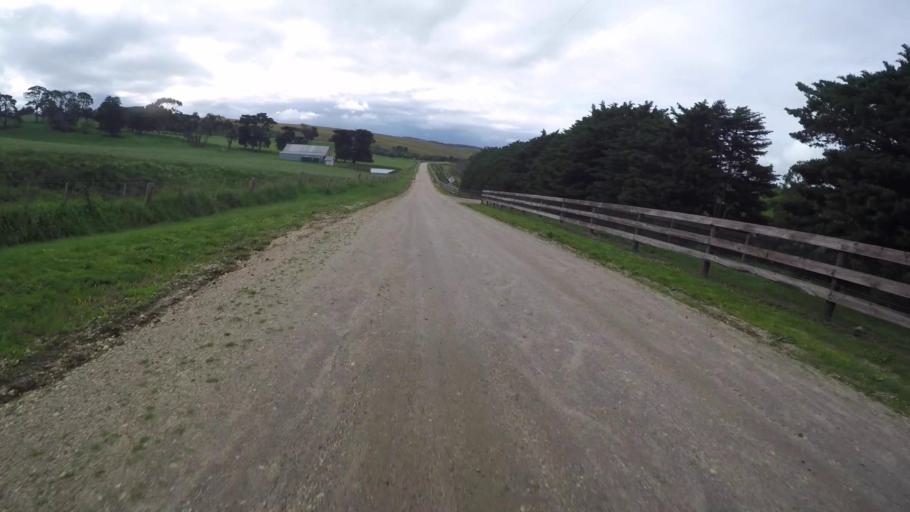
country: AU
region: Victoria
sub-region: Greater Geelong
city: Wandana Heights
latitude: -38.1772
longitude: 144.2361
